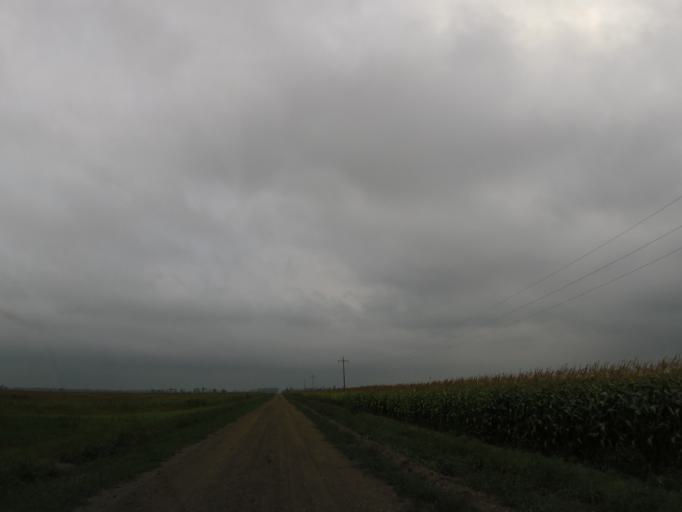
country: US
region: North Dakota
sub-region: Walsh County
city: Grafton
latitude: 48.5325
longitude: -97.1688
